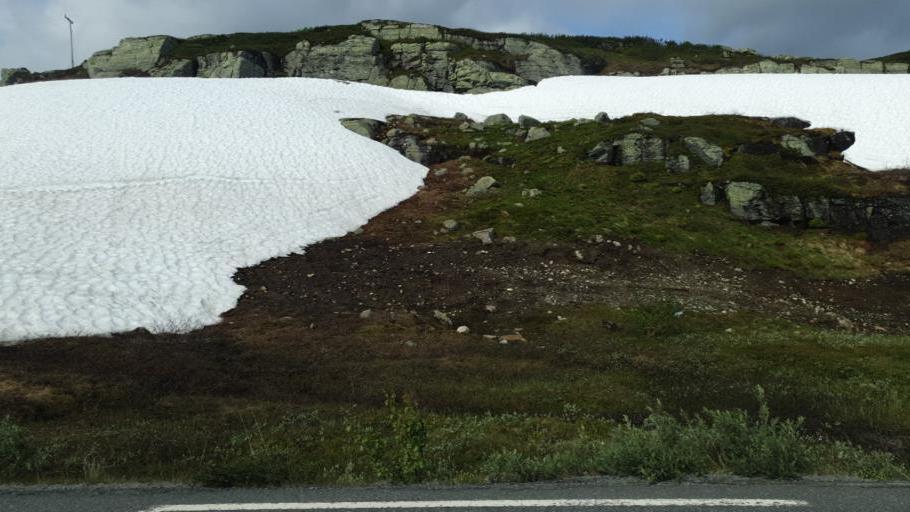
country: NO
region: Oppland
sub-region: Vestre Slidre
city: Slidre
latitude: 61.3137
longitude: 8.8080
